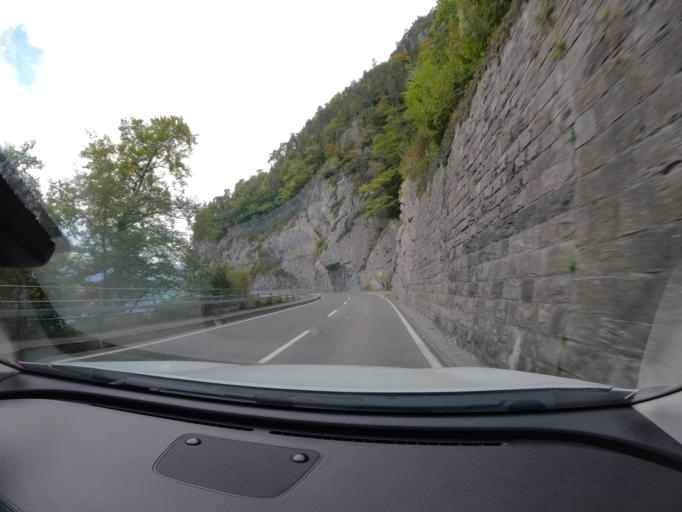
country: CH
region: Bern
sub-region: Interlaken-Oberhasli District
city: Beatenberg
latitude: 46.6855
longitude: 7.7885
